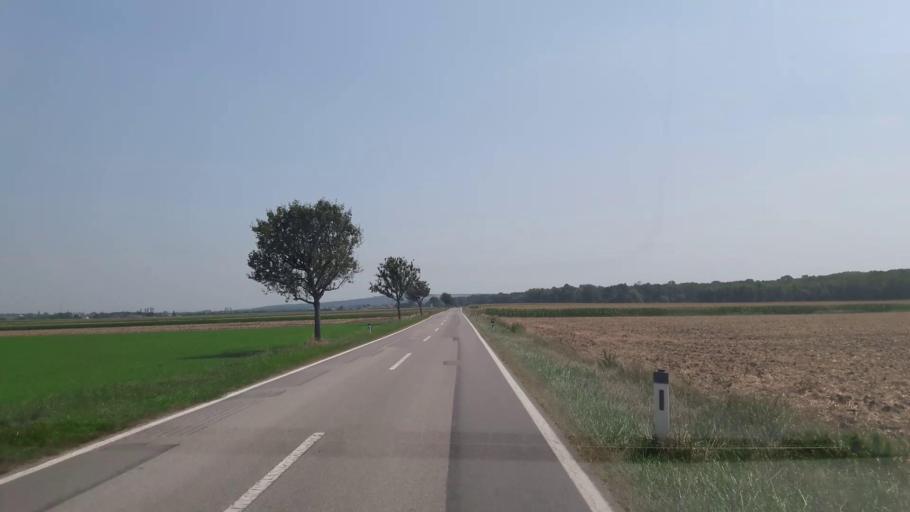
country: AT
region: Lower Austria
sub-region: Politischer Bezirk Bruck an der Leitha
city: Sommerein
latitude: 48.0192
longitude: 16.6932
